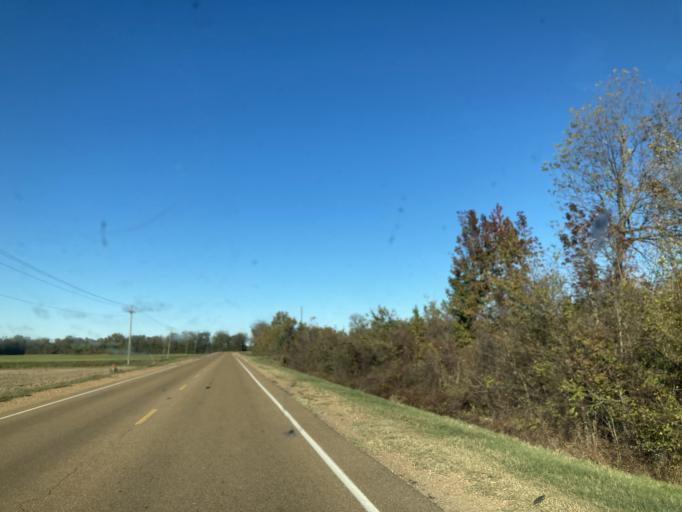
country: US
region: Mississippi
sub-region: Yazoo County
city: Yazoo City
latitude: 32.8100
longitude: -90.4532
